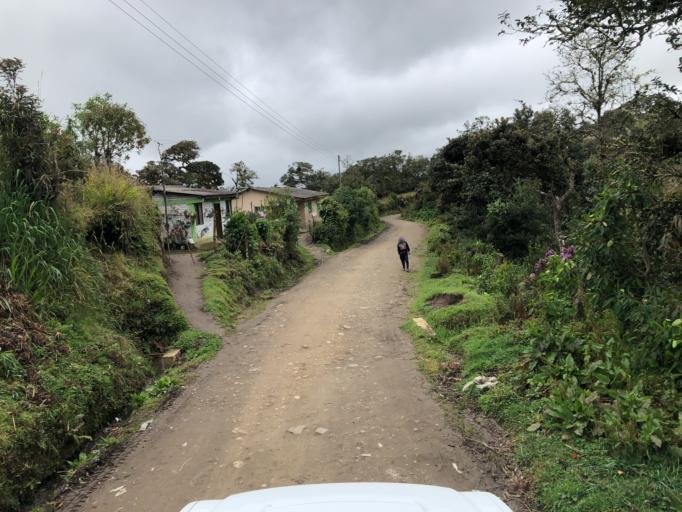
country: CO
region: Cauca
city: Totoro
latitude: 2.4917
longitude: -76.3447
